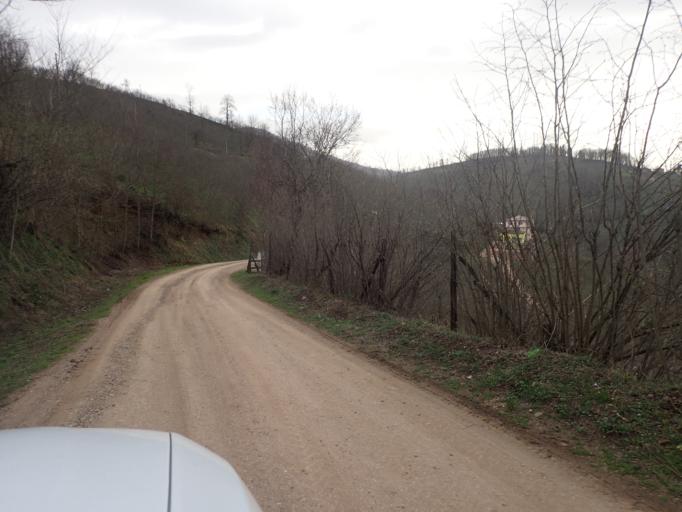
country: TR
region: Ordu
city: Camas
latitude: 40.8899
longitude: 37.4984
